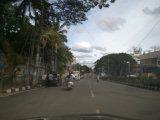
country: IN
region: Karnataka
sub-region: Bangalore Urban
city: Bangalore
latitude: 12.9802
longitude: 77.5380
